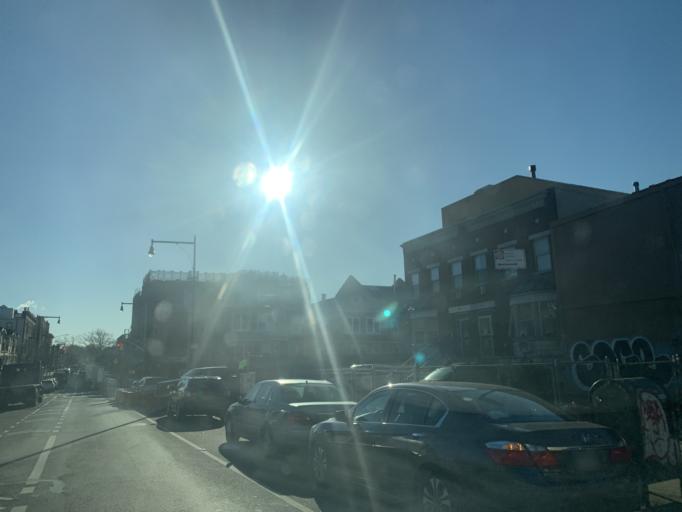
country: US
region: New York
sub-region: Kings County
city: East New York
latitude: 40.6984
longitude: -73.9133
